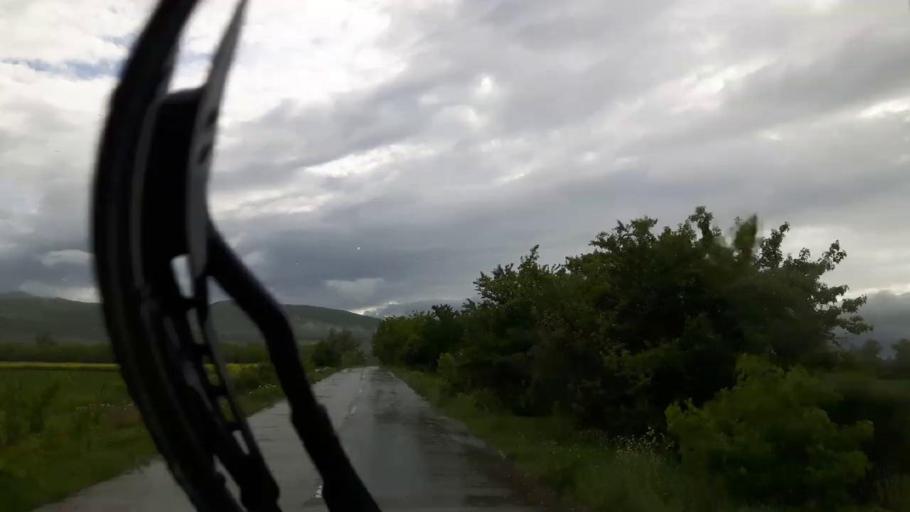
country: GE
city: Agara
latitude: 41.9956
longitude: 43.7456
